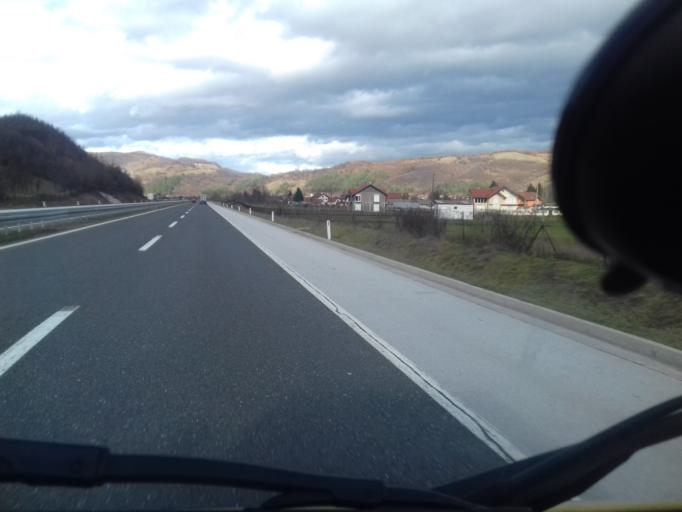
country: BA
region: Federation of Bosnia and Herzegovina
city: Mahala
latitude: 43.9816
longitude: 18.2331
